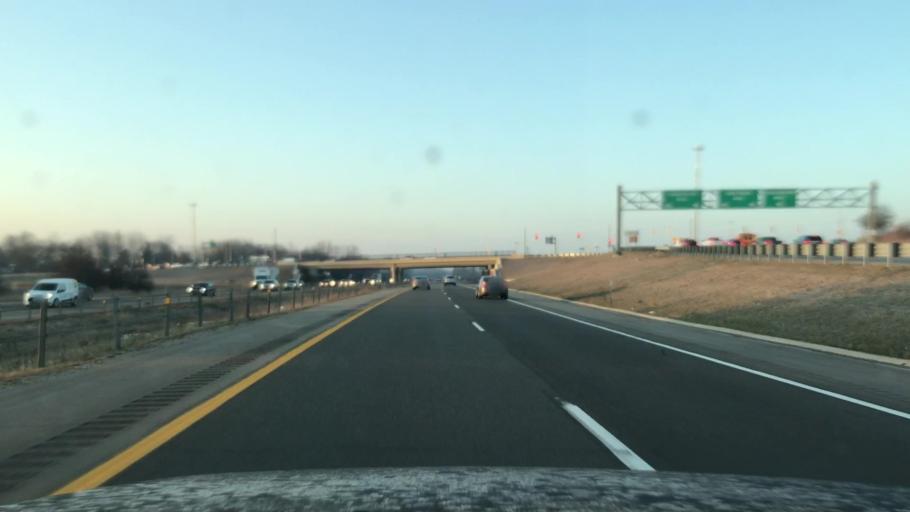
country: US
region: Michigan
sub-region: Kent County
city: East Grand Rapids
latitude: 42.9490
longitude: -85.5674
